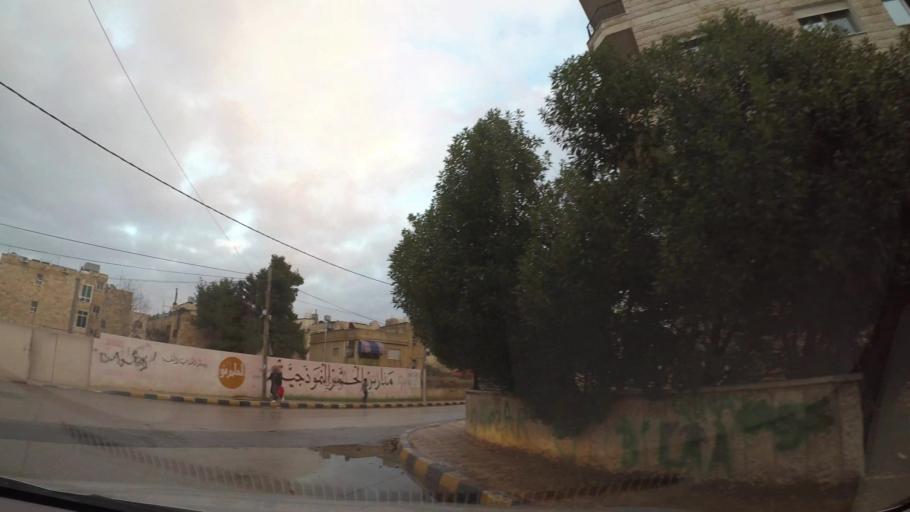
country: JO
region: Amman
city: Al Jubayhah
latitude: 32.0308
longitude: 35.8250
